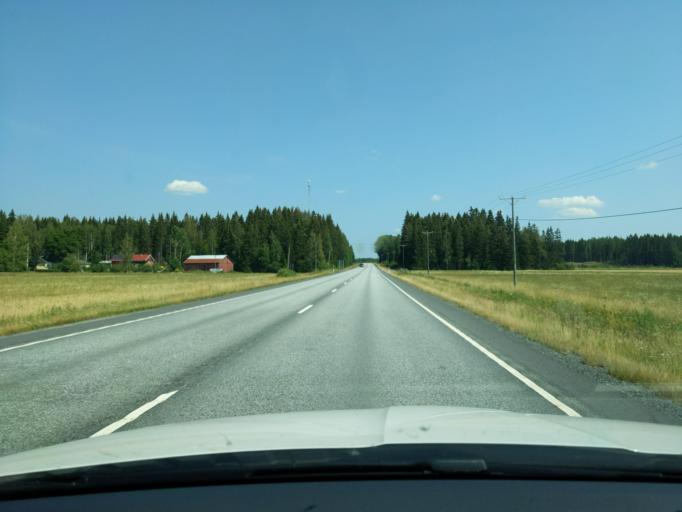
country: FI
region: Haeme
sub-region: Forssa
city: Ypaejae
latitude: 60.7345
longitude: 23.2562
